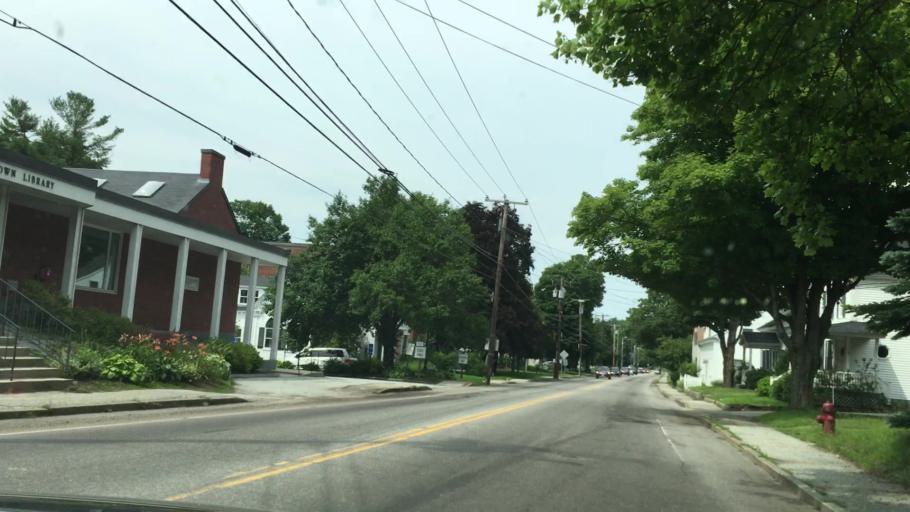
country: US
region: New Hampshire
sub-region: Hillsborough County
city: Peterborough
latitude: 42.8777
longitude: -71.9479
